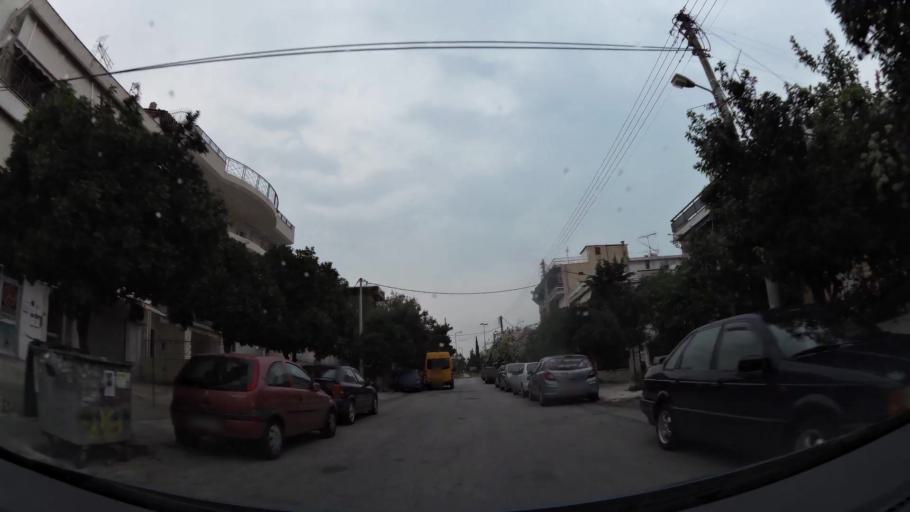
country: GR
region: Attica
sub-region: Nomarchia Athinas
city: Argyroupoli
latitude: 37.9106
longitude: 23.7440
